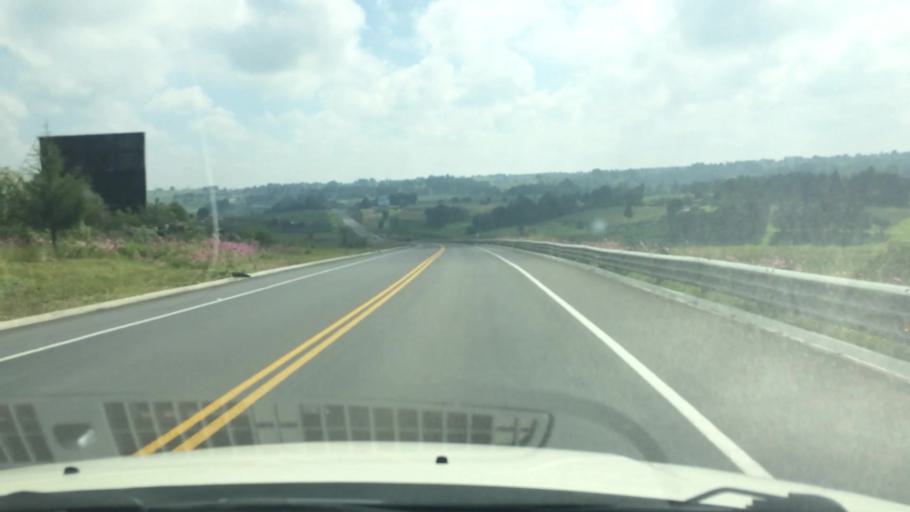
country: MX
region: Mexico
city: Amanalco de Becerra
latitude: 19.3553
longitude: -99.9711
